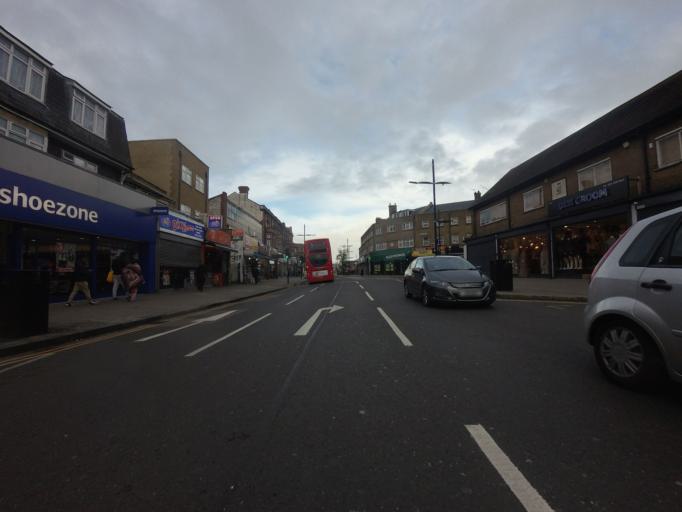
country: GB
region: England
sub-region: Greater London
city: East Ham
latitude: 51.5371
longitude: 0.0346
